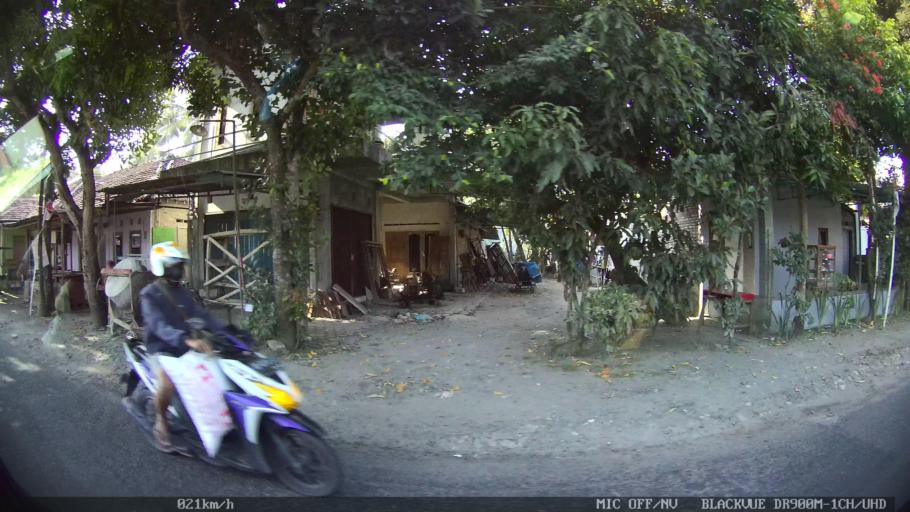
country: ID
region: Daerah Istimewa Yogyakarta
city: Bantul
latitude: -7.8812
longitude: 110.3108
